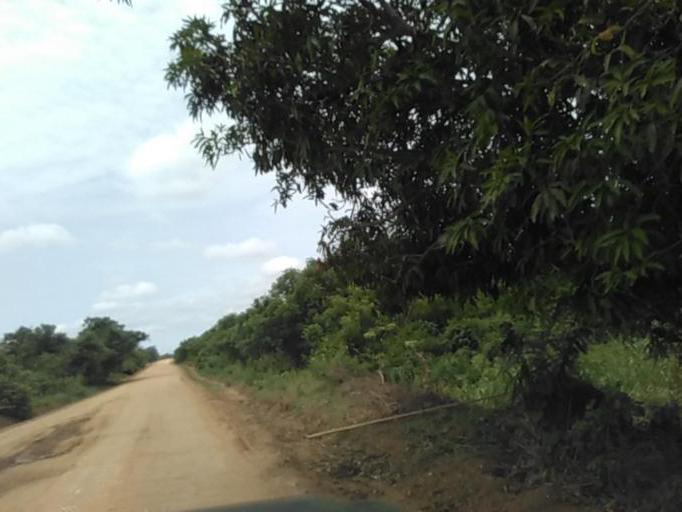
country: GH
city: Akropong
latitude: 6.0464
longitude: 0.2974
